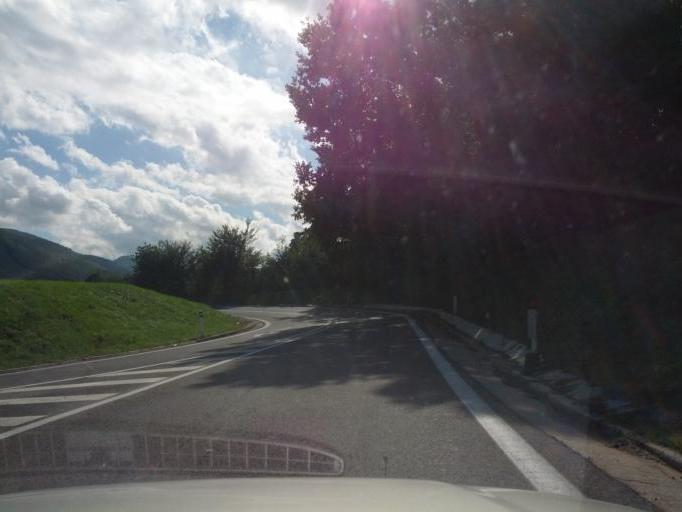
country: IT
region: Campania
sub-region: Provincia di Caserta
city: Bivio Mortola
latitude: 41.4326
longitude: 13.8970
